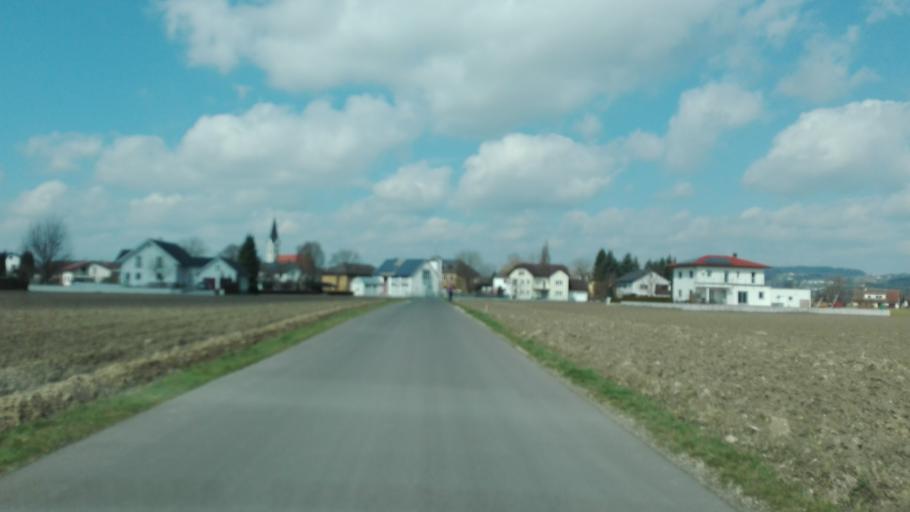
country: AT
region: Upper Austria
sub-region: Politischer Bezirk Urfahr-Umgebung
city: Goldworth
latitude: 48.3250
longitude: 14.1037
